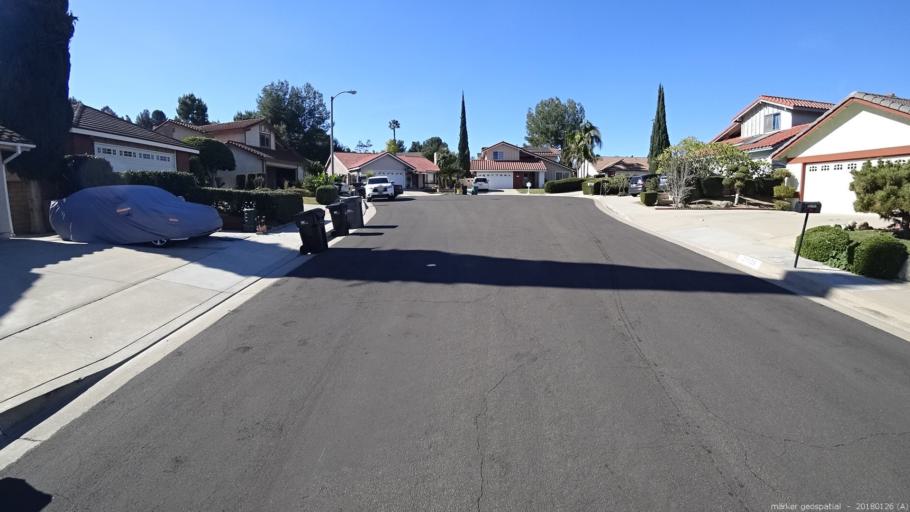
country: US
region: California
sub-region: Los Angeles County
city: Walnut
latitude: 33.9968
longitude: -117.8438
